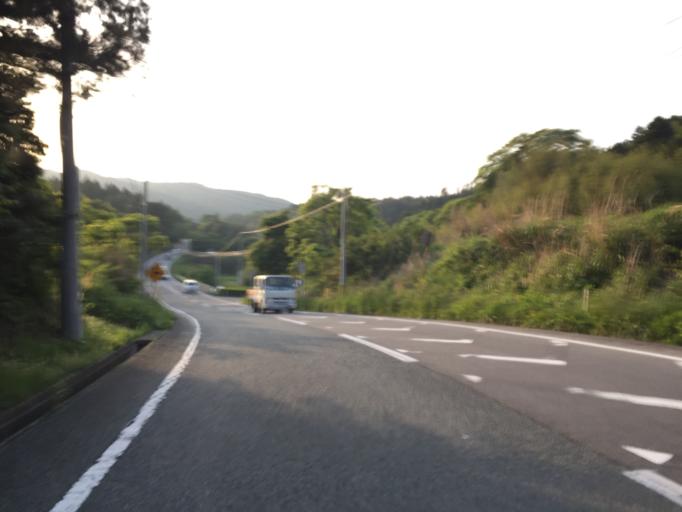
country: JP
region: Fukushima
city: Iwaki
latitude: 37.2390
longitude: 140.9773
